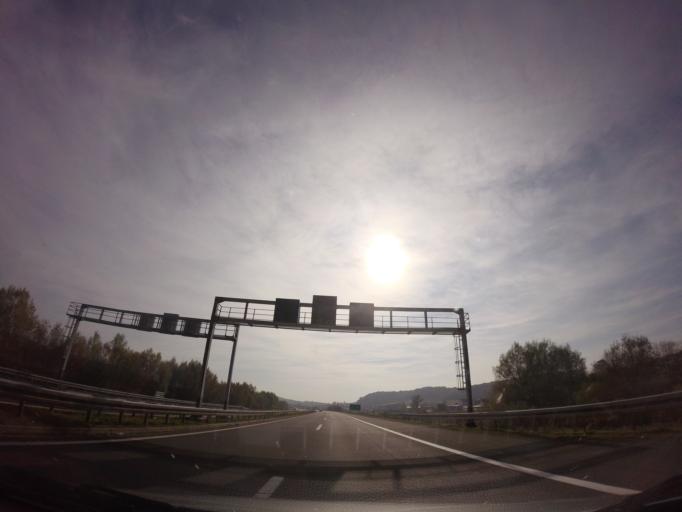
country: HR
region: Varazdinska
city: Remetinec
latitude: 46.0935
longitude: 16.2833
